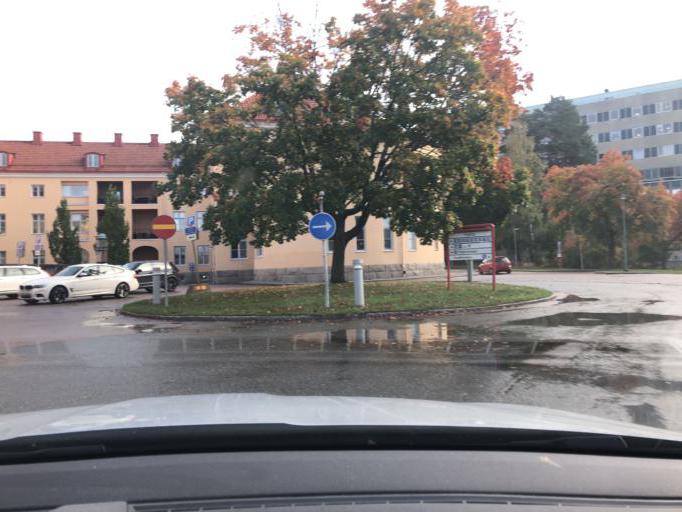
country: SE
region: Vaestmanland
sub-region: Vasteras
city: Vasteras
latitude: 59.6181
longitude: 16.5809
